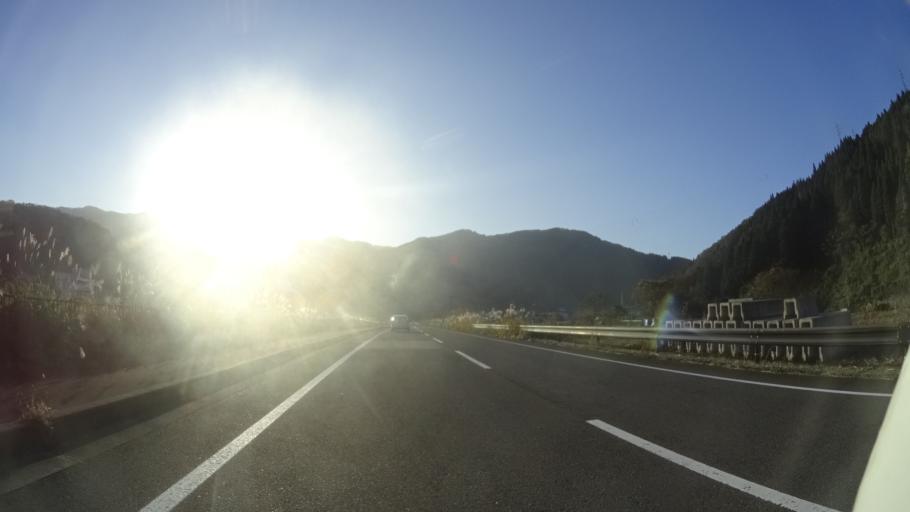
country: JP
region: Fukui
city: Ono
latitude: 35.9980
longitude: 136.3699
